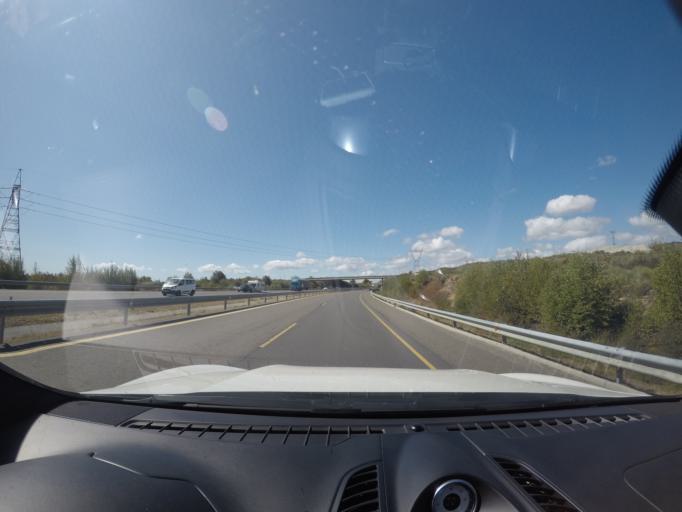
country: ES
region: Castille and Leon
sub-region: Provincia de Zamora
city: Pias
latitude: 42.0483
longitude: -7.0832
